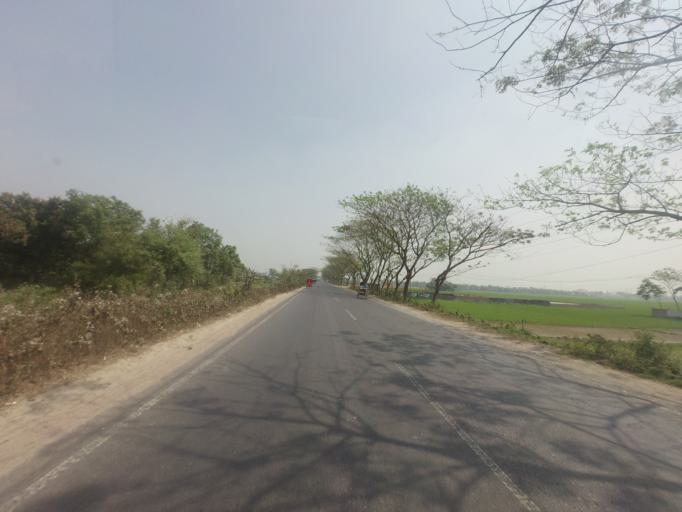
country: BD
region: Dhaka
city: Bhairab Bazar
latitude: 24.0494
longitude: 91.1060
